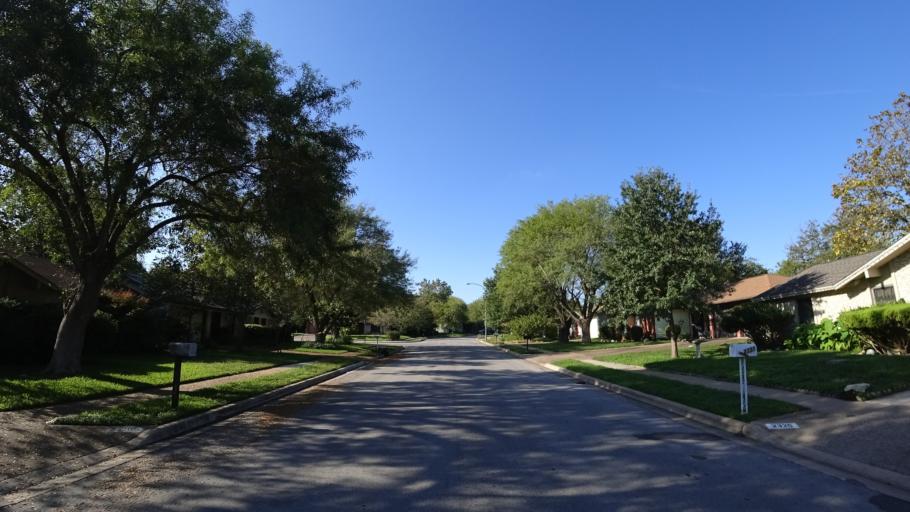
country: US
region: Texas
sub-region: Travis County
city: Shady Hollow
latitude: 30.2077
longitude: -97.8091
